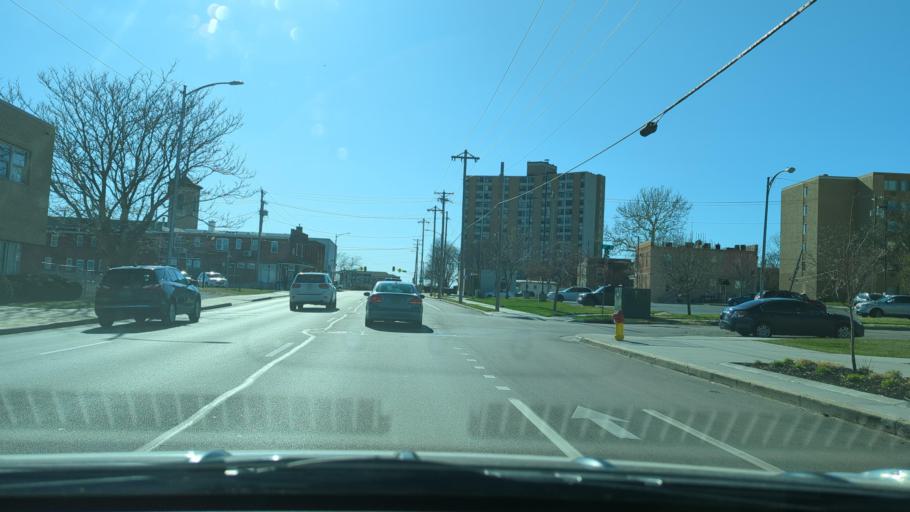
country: US
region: Nebraska
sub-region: Douglas County
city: Omaha
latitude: 41.2538
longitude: -95.9495
